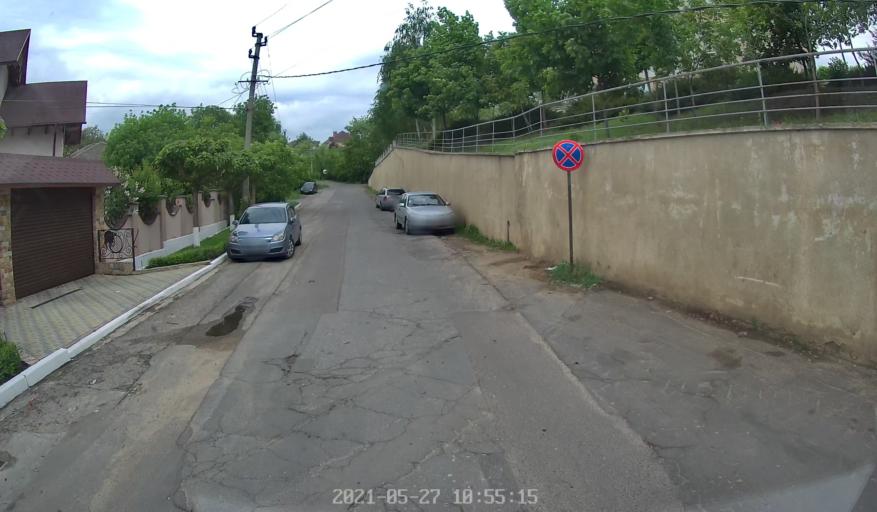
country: MD
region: Chisinau
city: Stauceni
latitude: 47.0957
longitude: 28.8677
